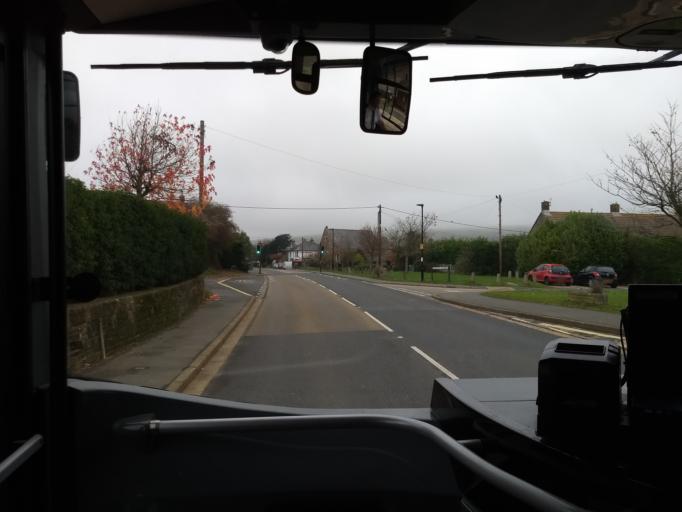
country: GB
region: England
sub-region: Isle of Wight
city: Newchurch
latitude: 50.6702
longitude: -1.2333
